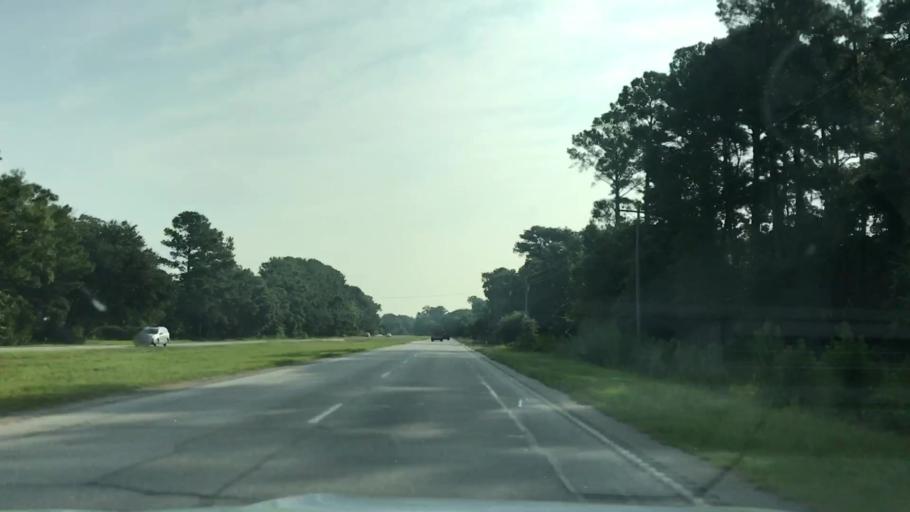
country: US
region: South Carolina
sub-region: Charleston County
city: Awendaw
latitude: 33.0714
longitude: -79.5190
